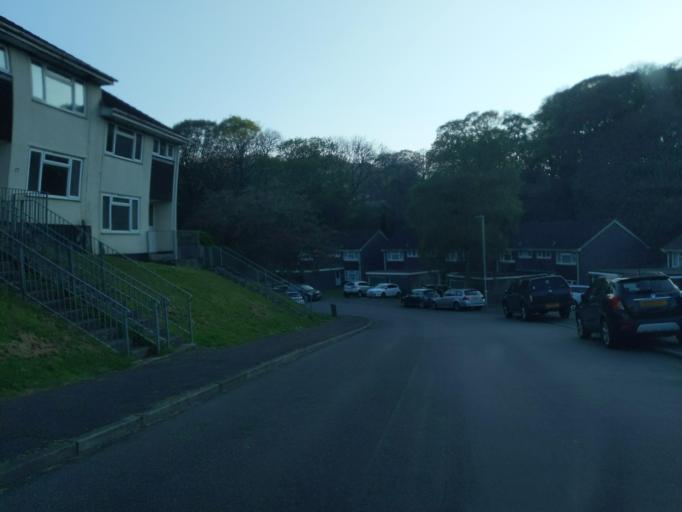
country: GB
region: England
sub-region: Plymouth
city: Plymstock
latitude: 50.3511
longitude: -4.0895
